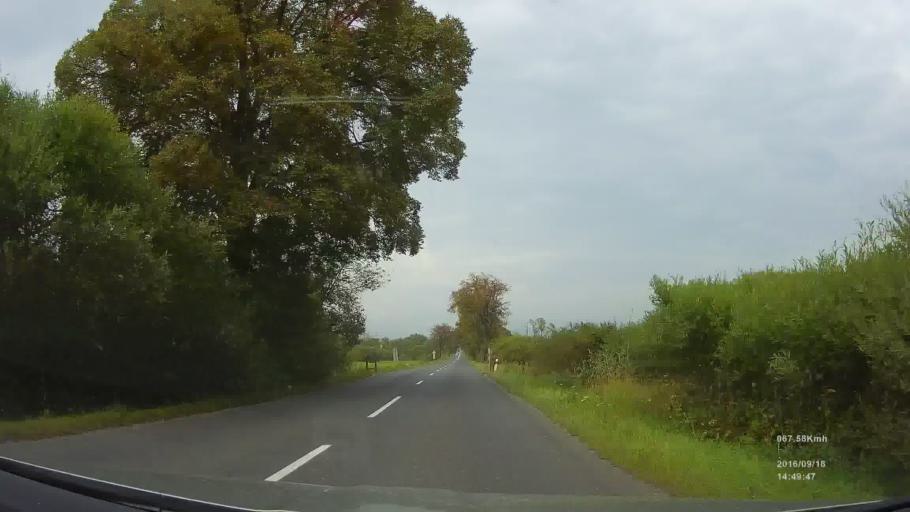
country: SK
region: Presovsky
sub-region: Okres Presov
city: Levoca
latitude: 48.9881
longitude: 20.5804
